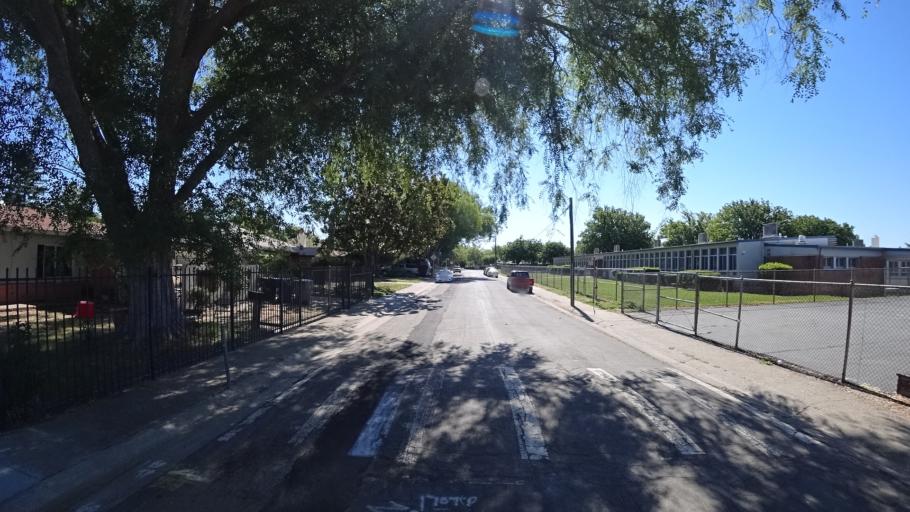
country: US
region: California
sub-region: Sacramento County
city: Parkway
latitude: 38.5312
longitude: -121.4400
